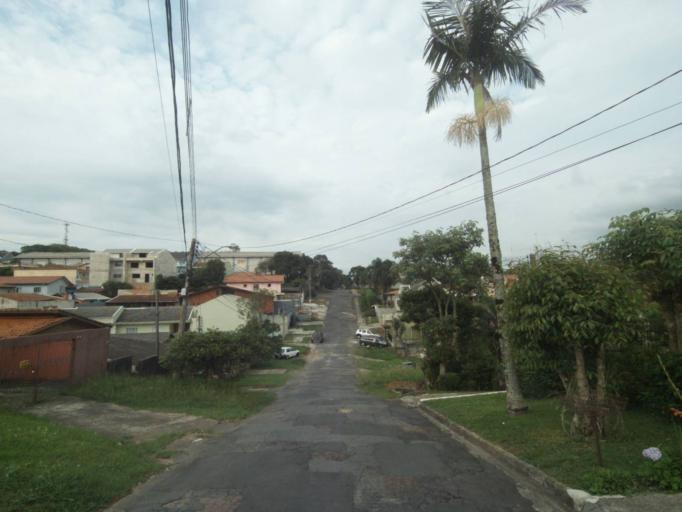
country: BR
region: Parana
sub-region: Curitiba
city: Curitiba
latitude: -25.3995
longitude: -49.2954
